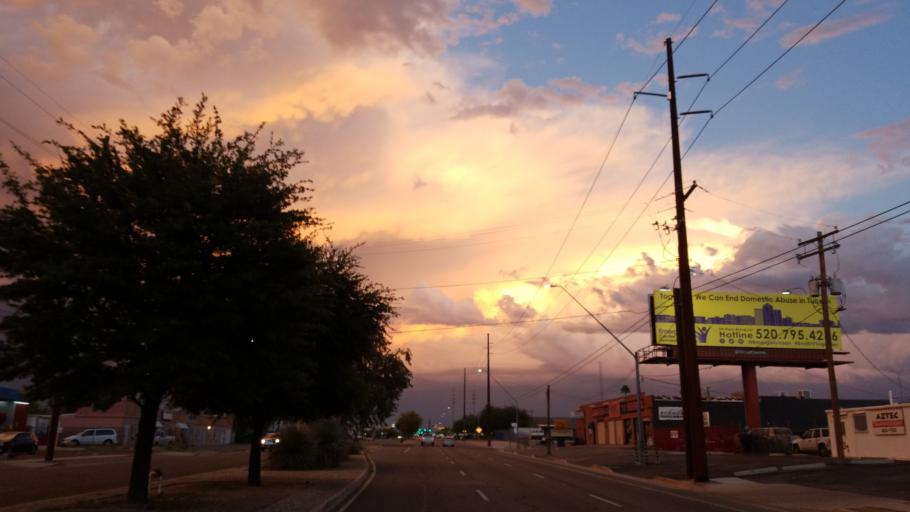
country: US
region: Arizona
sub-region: Pima County
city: Flowing Wells
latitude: 32.2502
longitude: -110.9856
